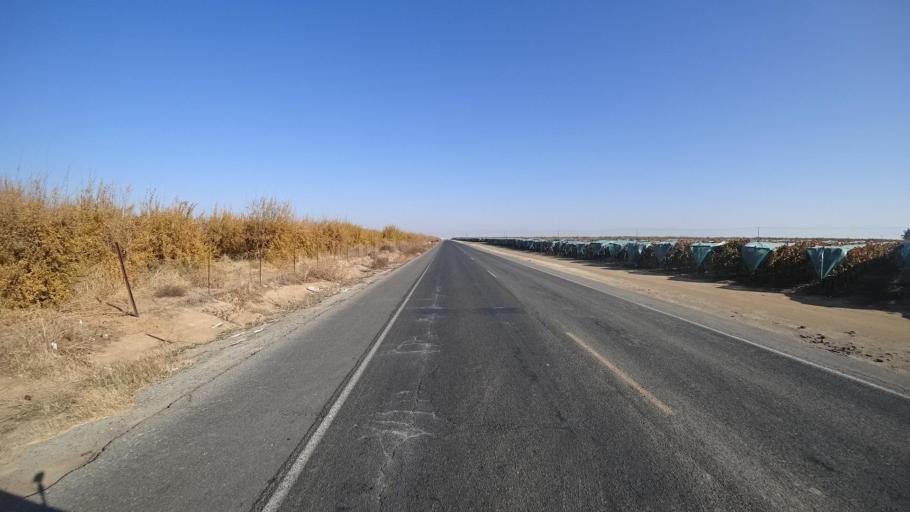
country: US
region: California
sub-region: Tulare County
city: Richgrove
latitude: 35.7543
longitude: -119.1373
